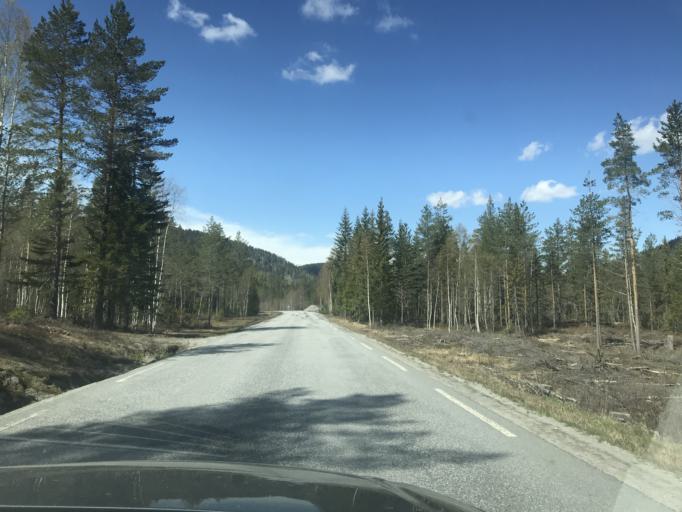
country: NO
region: Telemark
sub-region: Hjartdal
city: Sauland
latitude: 59.6956
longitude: 8.8667
